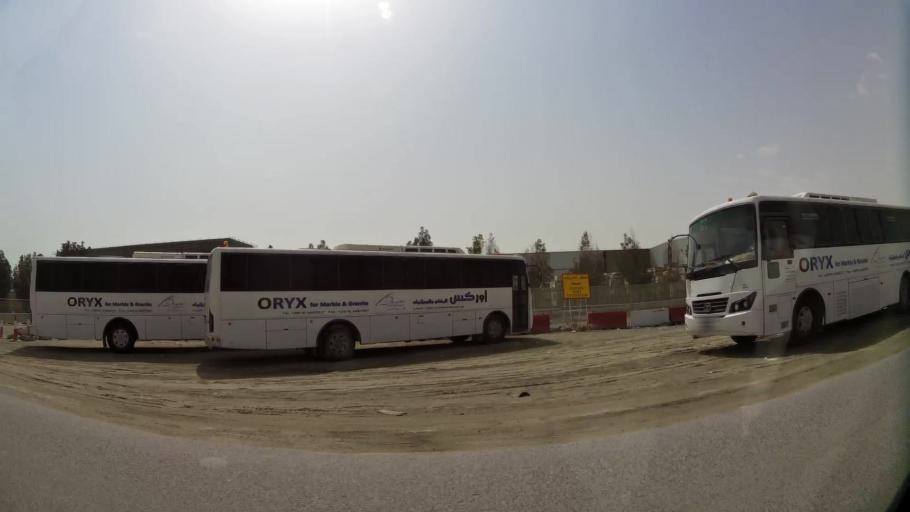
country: QA
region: Al Wakrah
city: Al Wukayr
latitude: 25.1665
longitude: 51.4454
